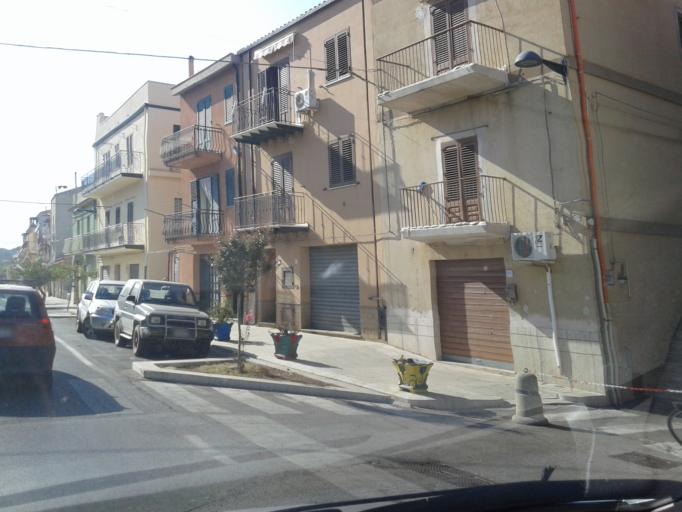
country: IT
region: Sicily
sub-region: Palermo
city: Finale
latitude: 38.0201
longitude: 14.1620
